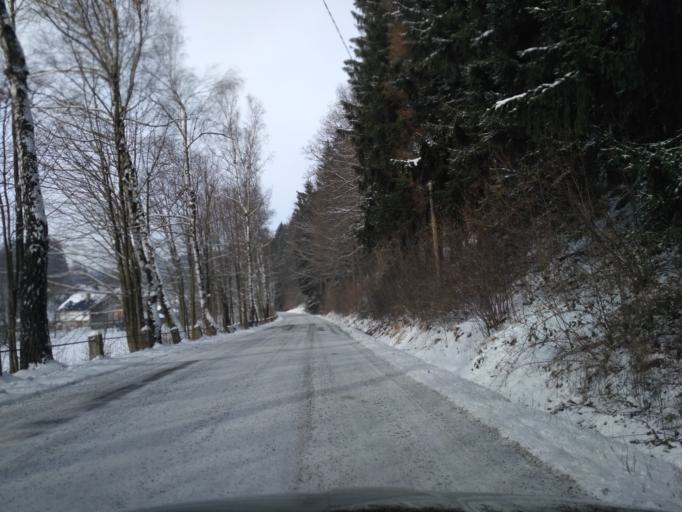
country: CZ
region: Zlin
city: Valasska Bystrice
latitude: 49.4070
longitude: 18.1303
